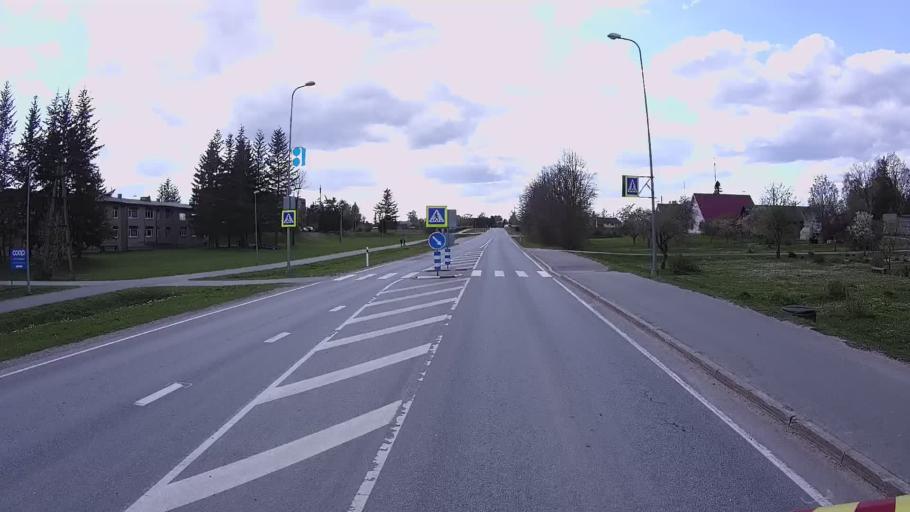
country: EE
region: Jogevamaa
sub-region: Mustvee linn
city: Mustvee
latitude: 58.8207
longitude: 26.7397
